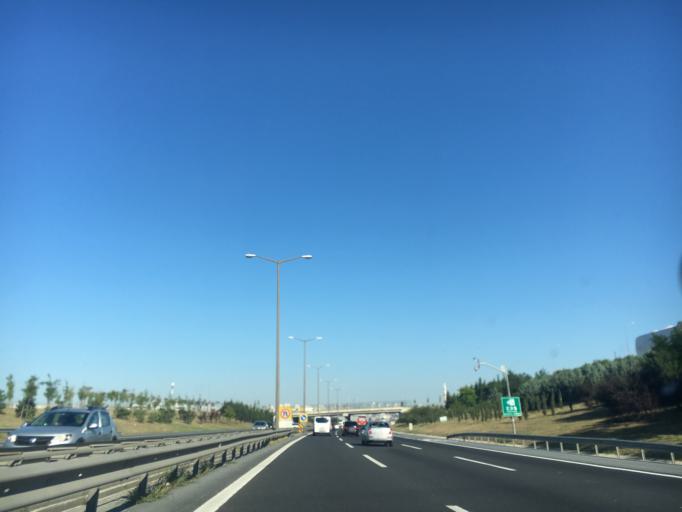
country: TR
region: Istanbul
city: Esenyurt
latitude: 41.0552
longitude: 28.6648
